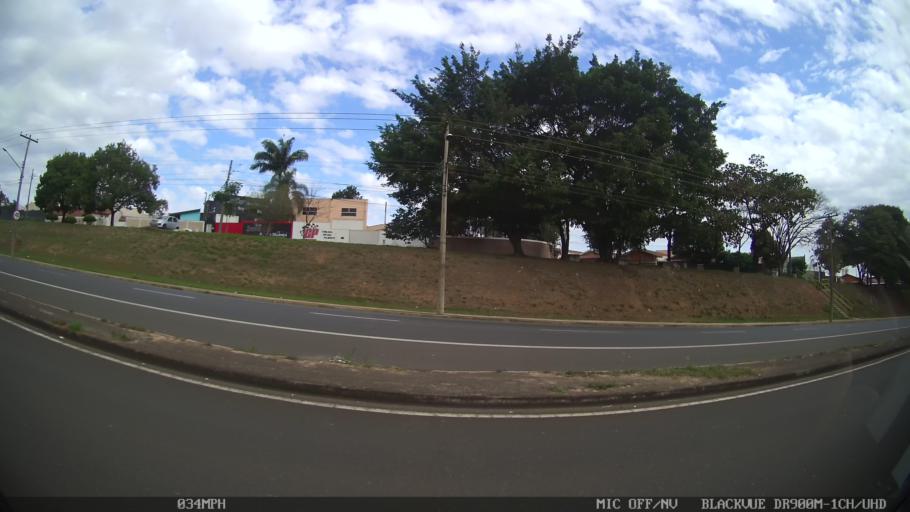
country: BR
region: Sao Paulo
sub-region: Limeira
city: Limeira
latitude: -22.5443
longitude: -47.3992
